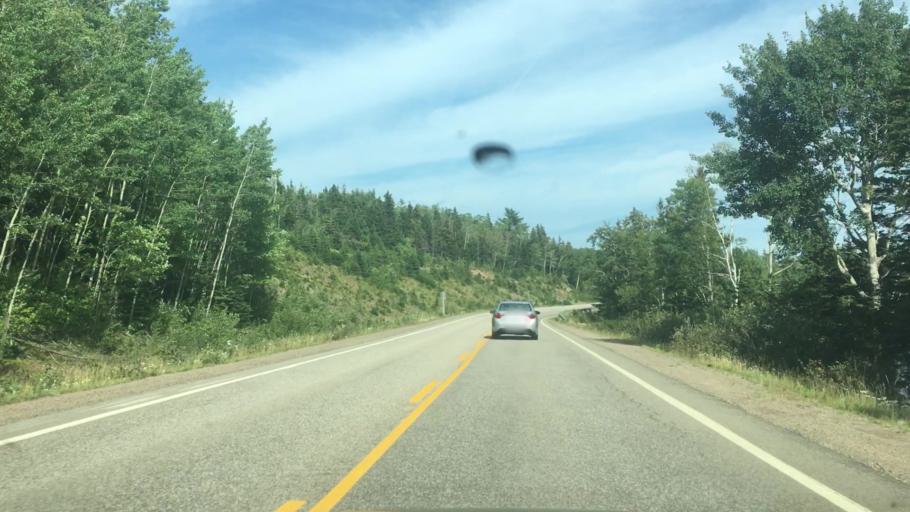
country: CA
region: Nova Scotia
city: Sydney Mines
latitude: 46.7136
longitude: -60.3584
